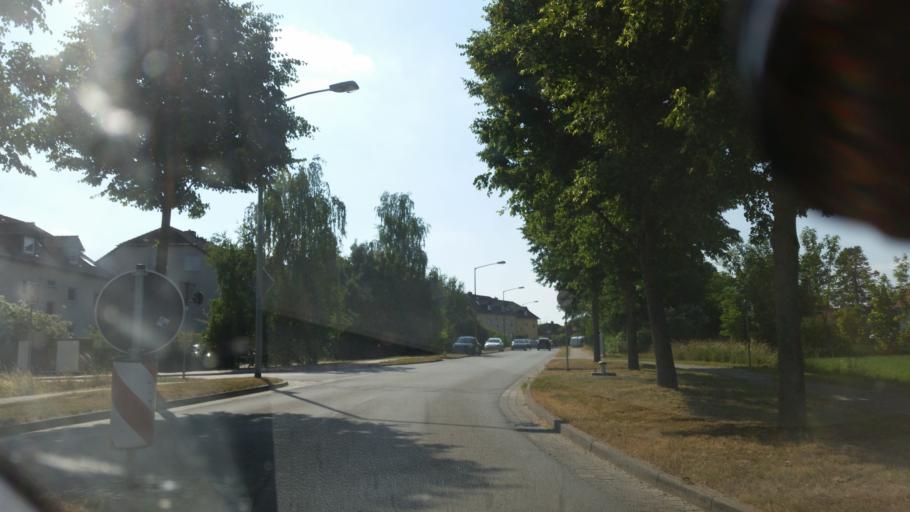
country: DE
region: Lower Saxony
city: Lehre
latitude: 52.3232
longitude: 10.6752
